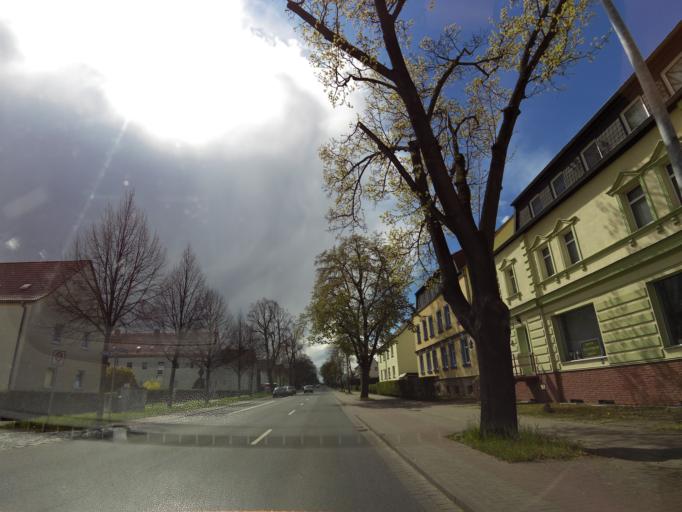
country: DE
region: Saxony-Anhalt
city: Diesdorf
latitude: 52.0946
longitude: 11.5723
